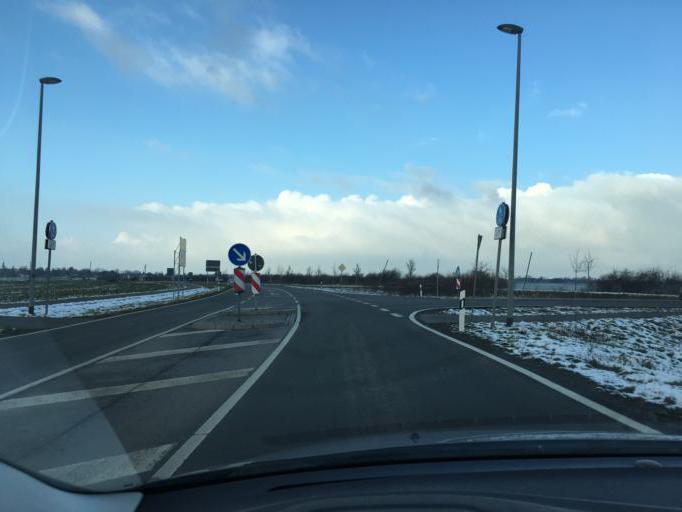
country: DE
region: Saxony
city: Brandis
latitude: 51.3438
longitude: 12.5974
